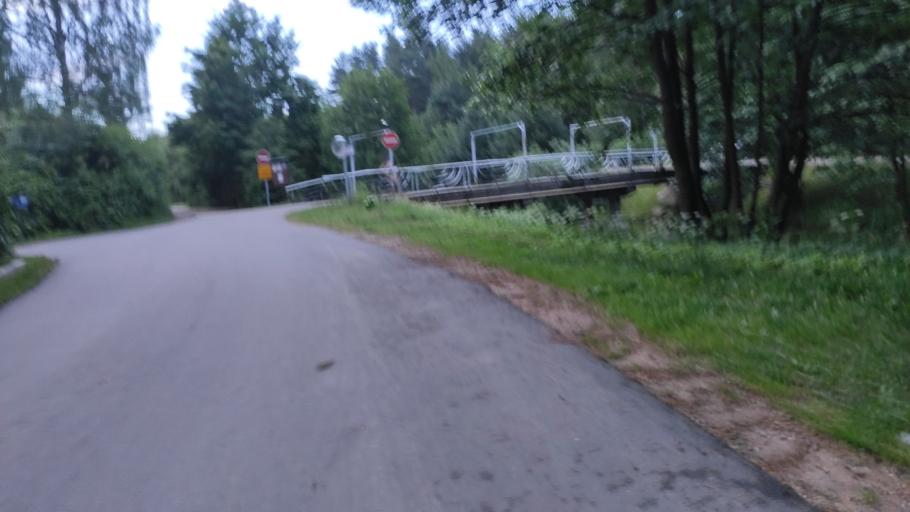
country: BY
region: Minsk
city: Zhdanovichy
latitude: 53.9670
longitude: 27.4431
